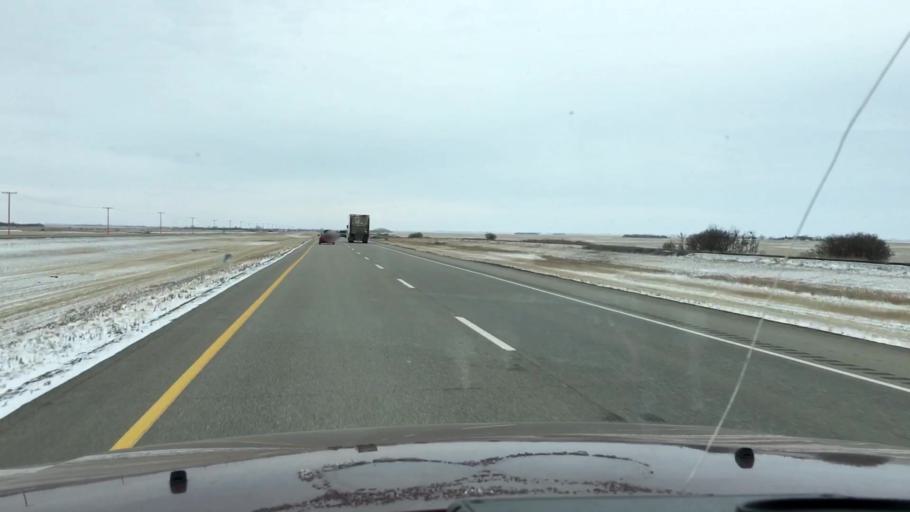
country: CA
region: Saskatchewan
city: Watrous
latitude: 51.1883
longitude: -105.9464
